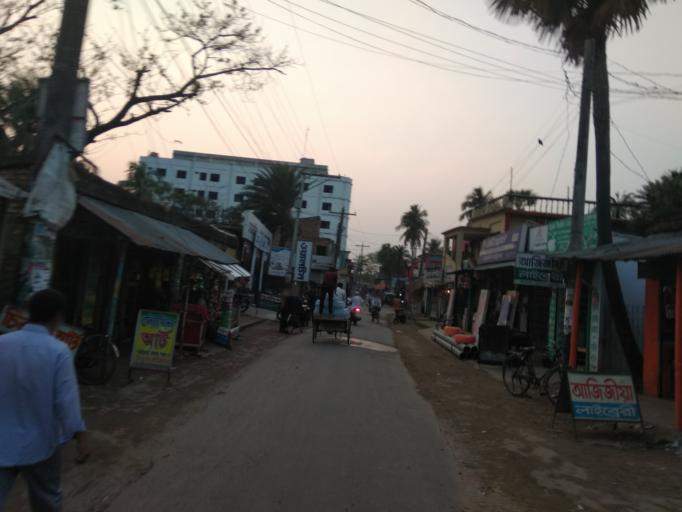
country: IN
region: West Bengal
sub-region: North 24 Parganas
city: Taki
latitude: 22.4546
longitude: 89.0334
